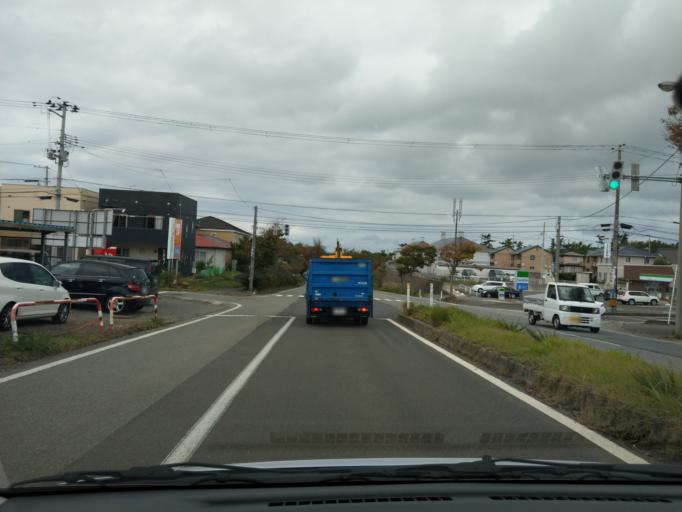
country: JP
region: Akita
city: Akita Shi
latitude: 39.6791
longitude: 140.0760
